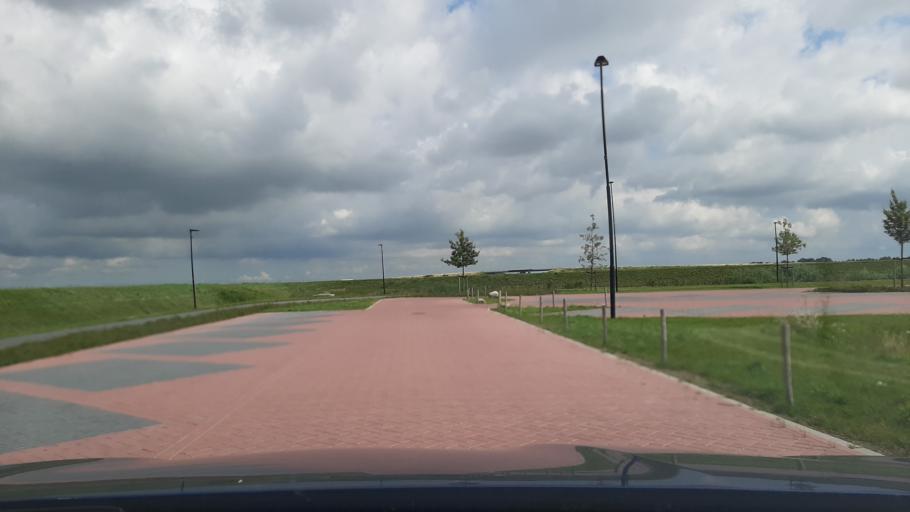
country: NL
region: Groningen
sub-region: Gemeente  Oldambt
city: Winschoten
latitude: 53.1847
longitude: 6.9567
